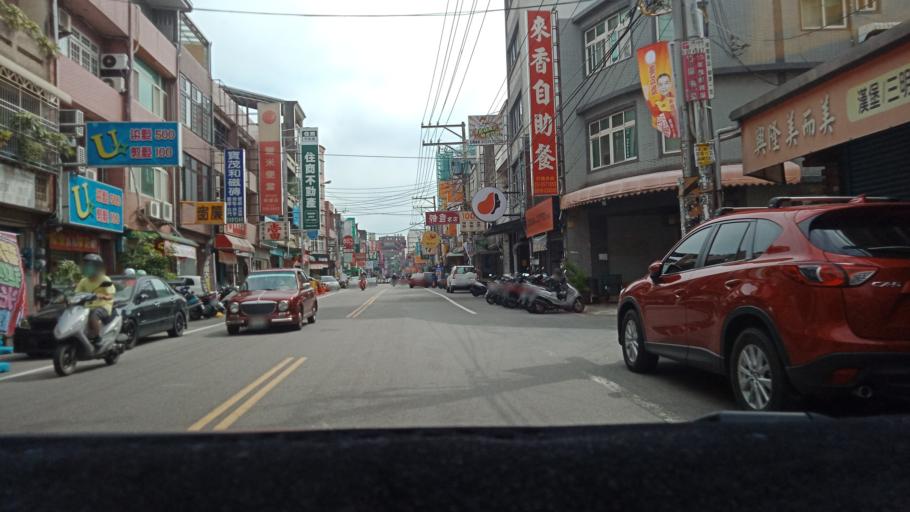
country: TW
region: Taiwan
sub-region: Hsinchu
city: Zhubei
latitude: 24.8745
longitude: 120.9946
